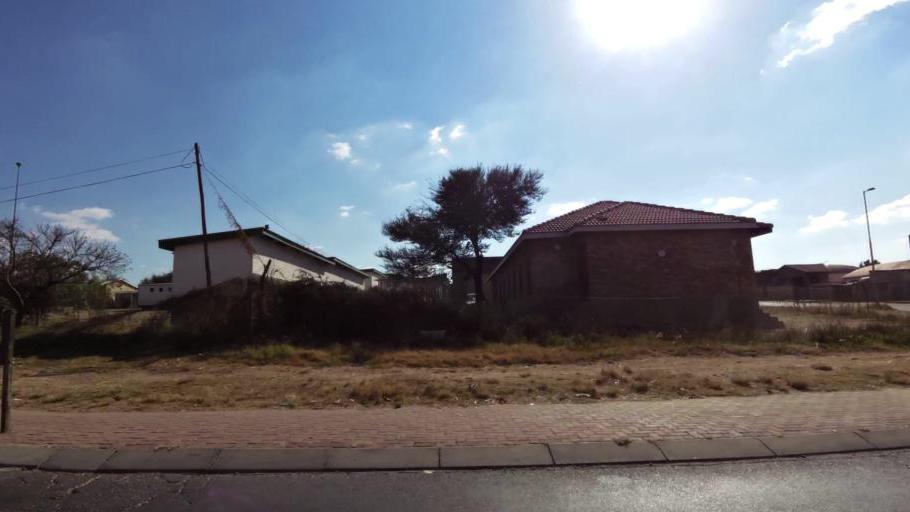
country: ZA
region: Gauteng
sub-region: City of Johannesburg Metropolitan Municipality
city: Soweto
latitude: -26.2269
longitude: 27.9182
